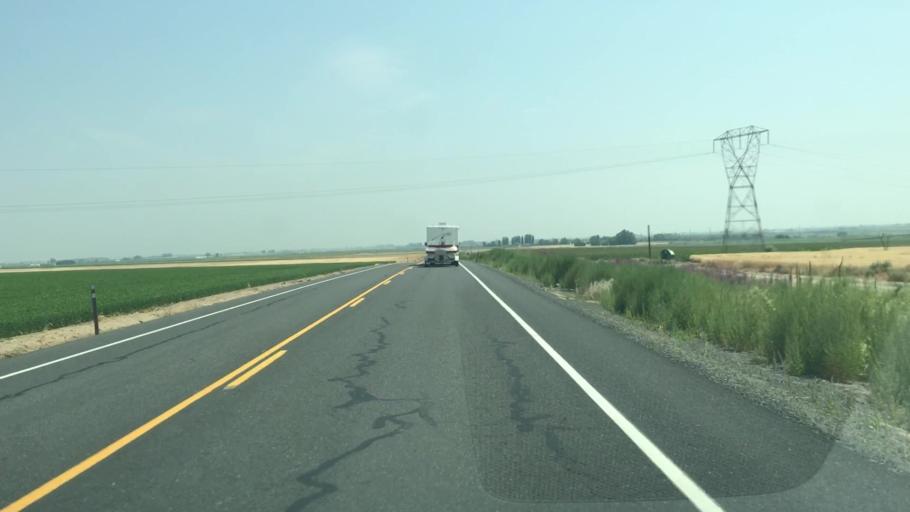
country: US
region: Washington
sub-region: Grant County
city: Quincy
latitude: 47.1639
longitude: -119.9348
